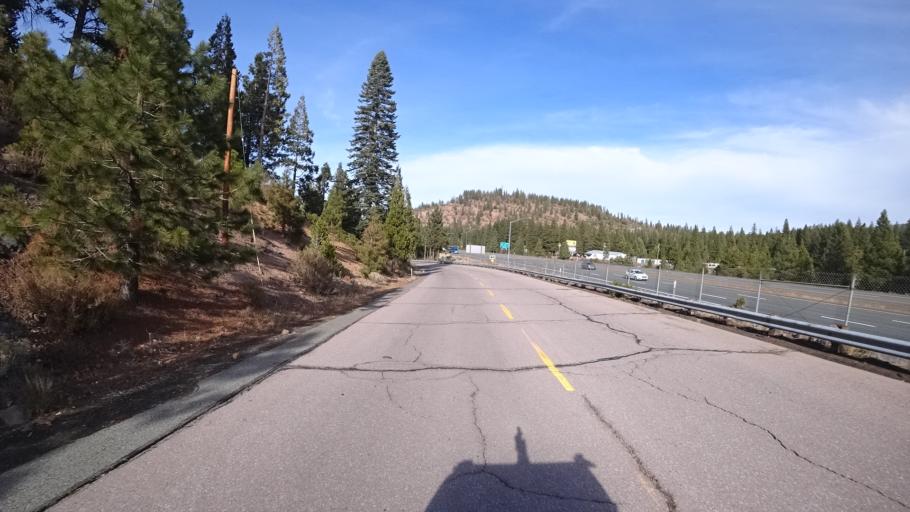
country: US
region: California
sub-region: Siskiyou County
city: Weed
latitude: 41.4088
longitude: -122.3804
